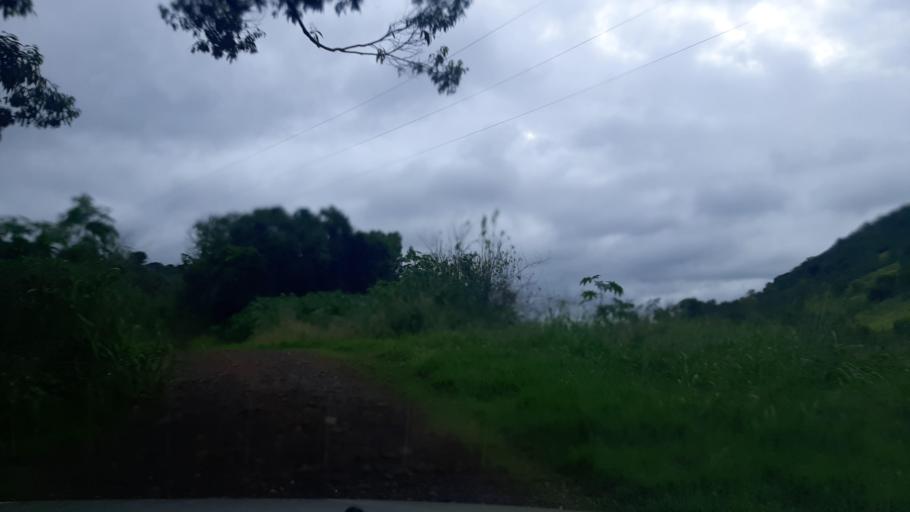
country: BR
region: Parana
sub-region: Ampere
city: Ampere
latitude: -26.0472
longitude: -53.5183
